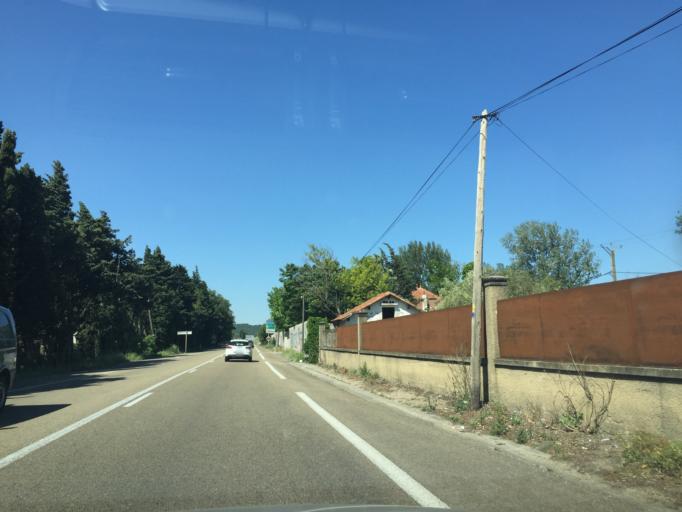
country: FR
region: Languedoc-Roussillon
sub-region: Departement du Gard
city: Saze
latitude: 43.9508
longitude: 4.7101
